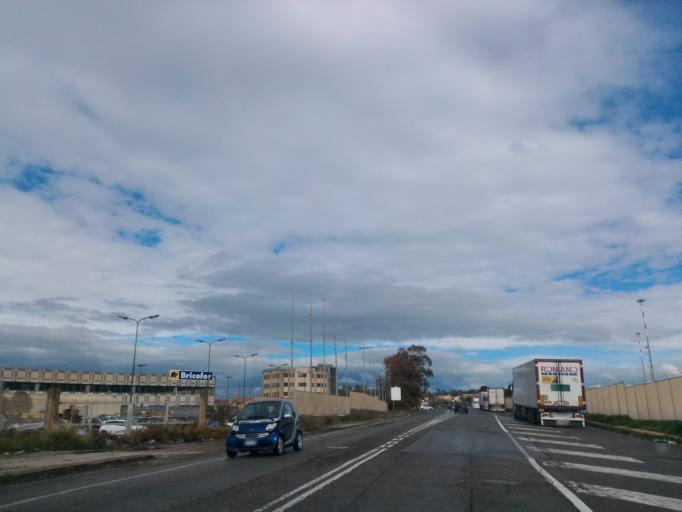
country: IT
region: Latium
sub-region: Citta metropolitana di Roma Capitale
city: Aurelia
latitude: 42.1244
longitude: 11.7710
